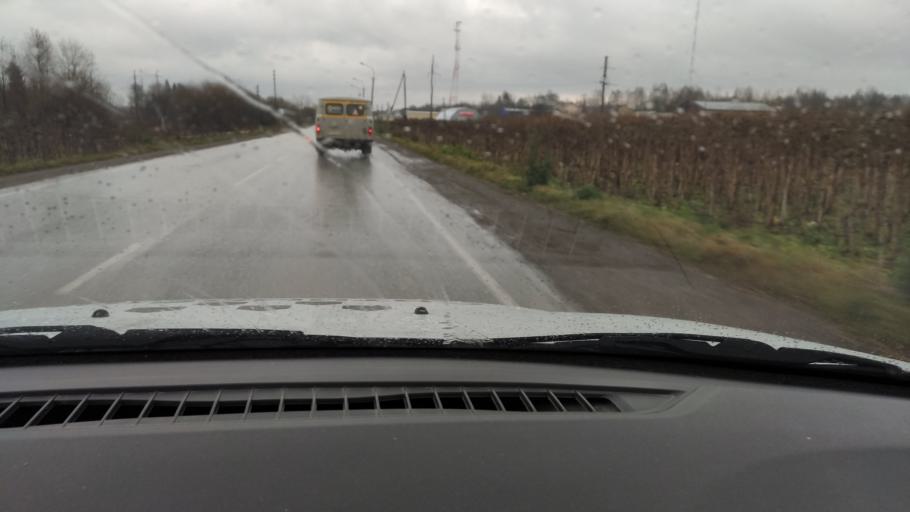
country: RU
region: Perm
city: Sylva
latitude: 58.0272
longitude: 56.7238
